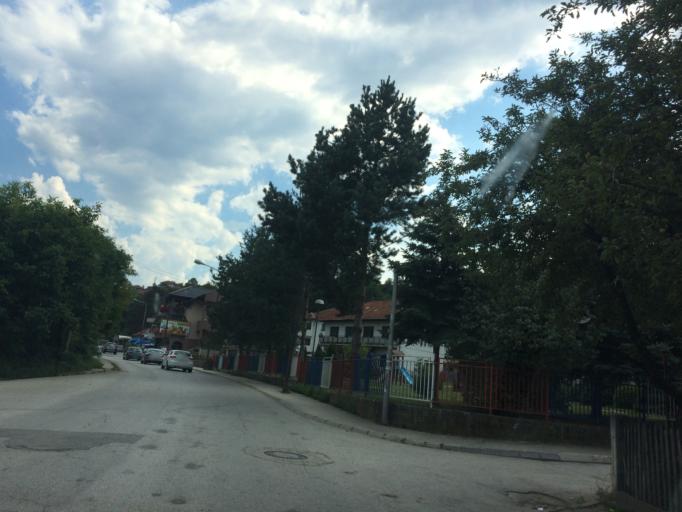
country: RS
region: Central Serbia
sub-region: Zlatiborski Okrug
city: Prijepolje
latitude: 43.3668
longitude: 19.6286
